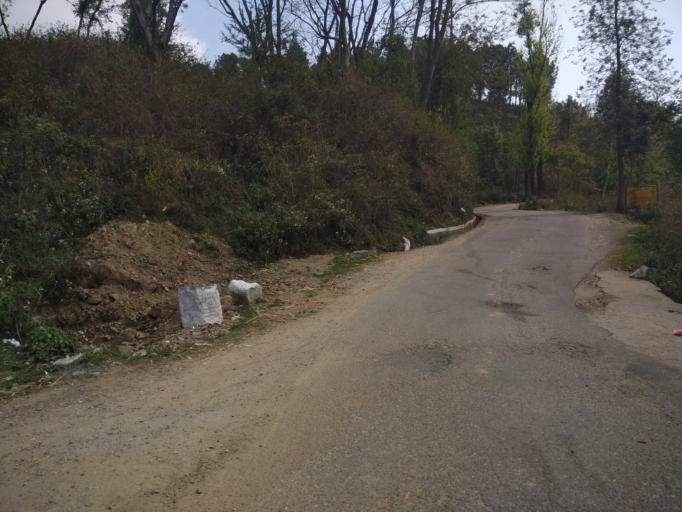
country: IN
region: Himachal Pradesh
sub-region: Kangra
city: Palampur
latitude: 32.0679
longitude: 76.6238
